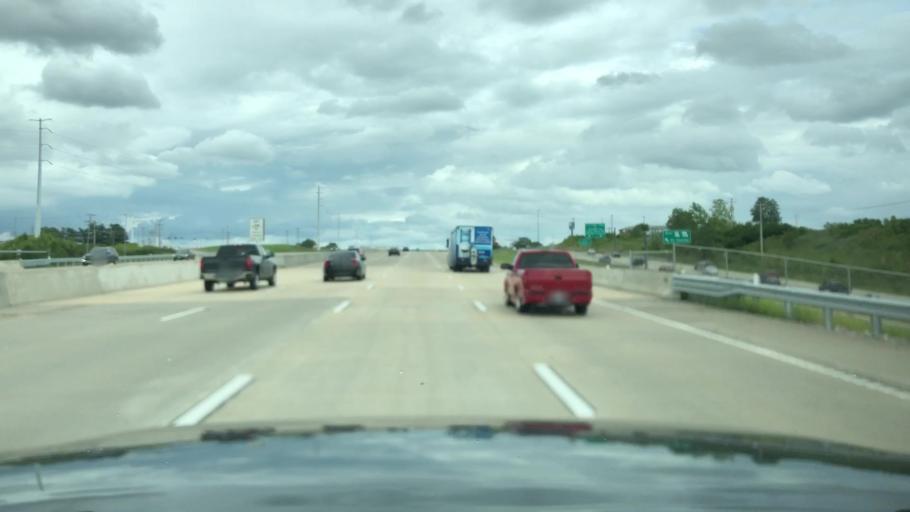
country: US
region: Missouri
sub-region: Saint Charles County
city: Saint Peters
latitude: 38.7479
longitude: -90.5845
